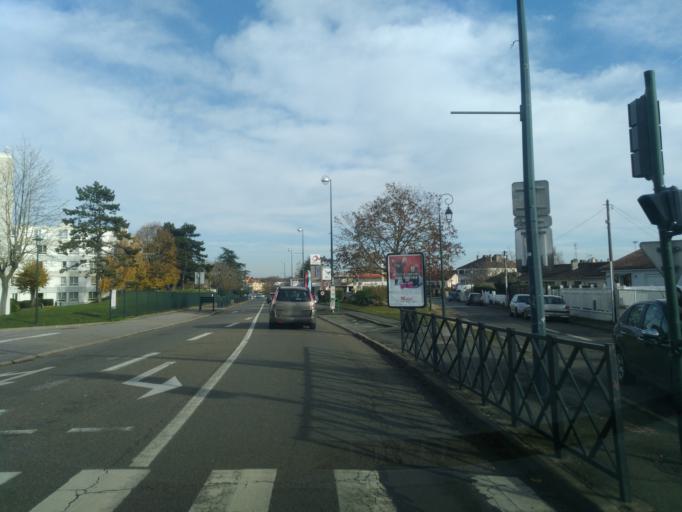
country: FR
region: Ile-de-France
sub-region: Departement des Yvelines
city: Villepreux
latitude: 48.8283
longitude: 1.9921
